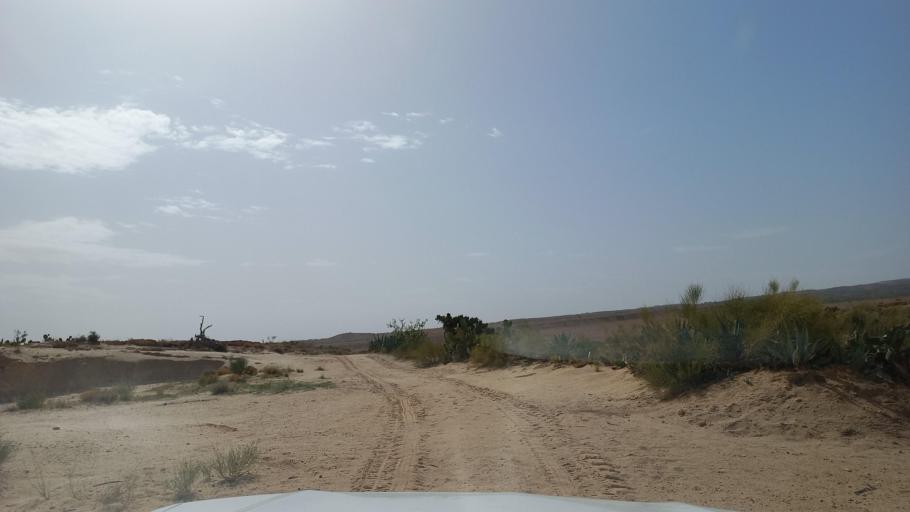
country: TN
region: Al Qasrayn
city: Kasserine
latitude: 35.2994
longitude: 8.9440
